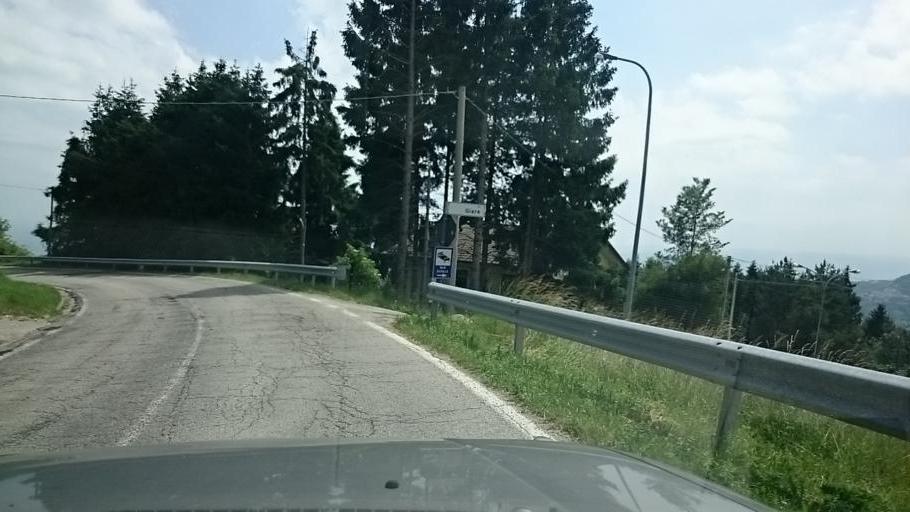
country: IT
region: Veneto
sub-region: Provincia di Vicenza
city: Conco
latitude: 45.8073
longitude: 11.6194
